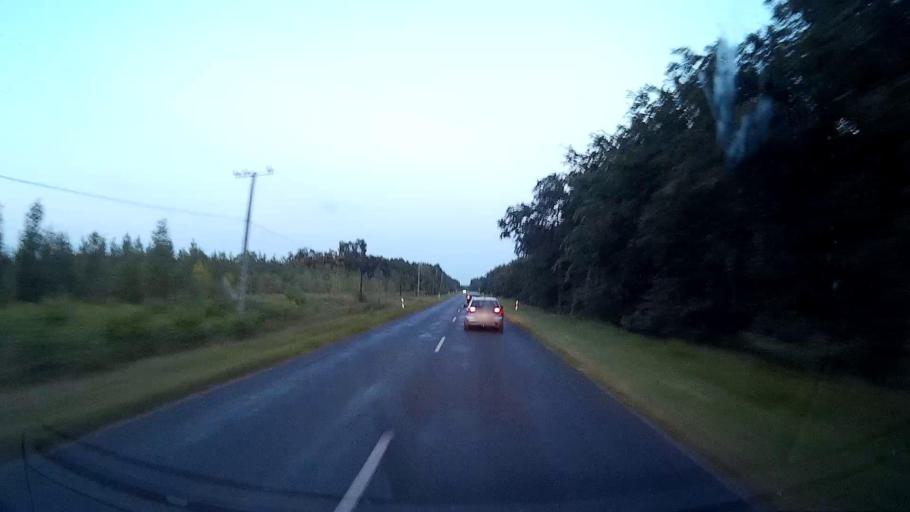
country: HU
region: Pest
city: Cegledbercel
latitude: 47.2041
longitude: 19.6954
